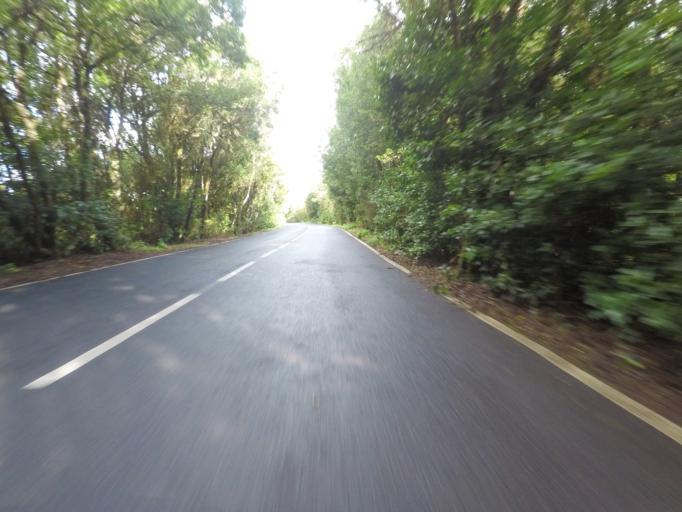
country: ES
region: Canary Islands
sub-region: Provincia de Santa Cruz de Tenerife
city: Hermigua
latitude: 28.1167
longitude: -17.2186
